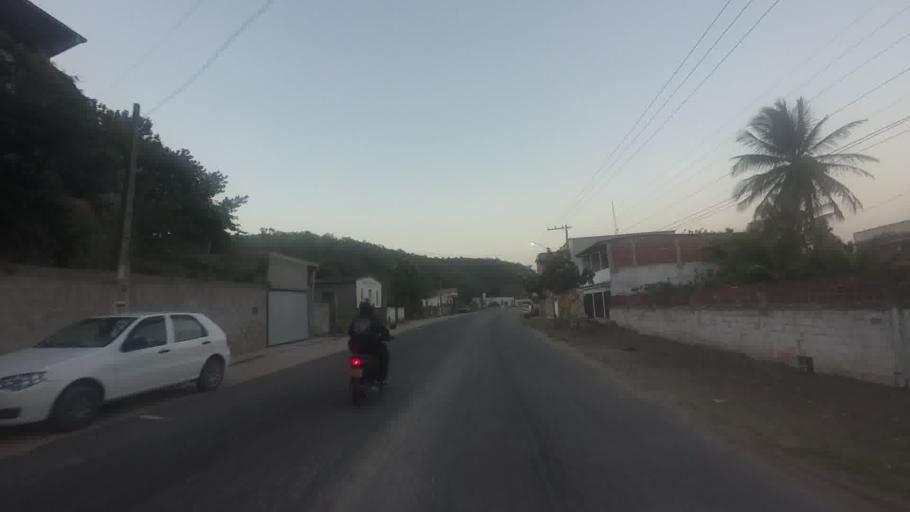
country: BR
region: Espirito Santo
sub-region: Piuma
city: Piuma
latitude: -20.8618
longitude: -40.7587
